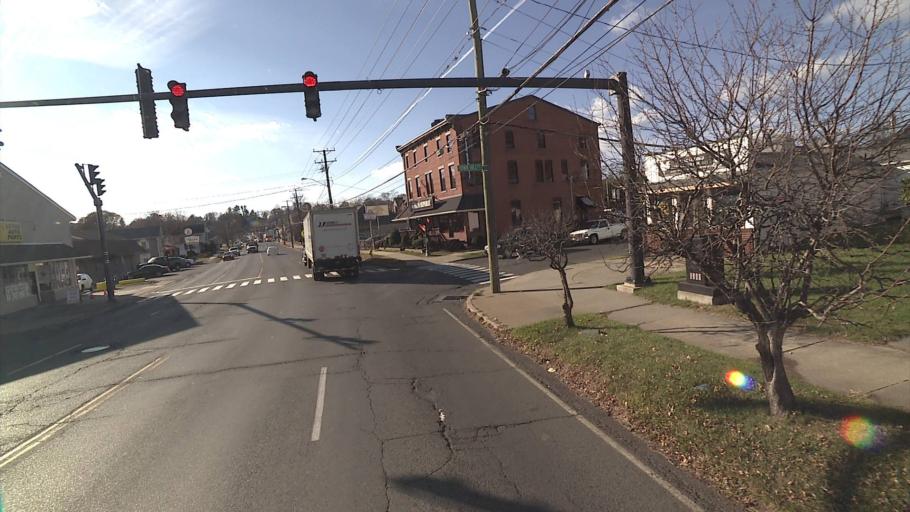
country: US
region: Connecticut
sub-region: Fairfield County
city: Danbury
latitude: 41.3876
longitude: -73.4415
